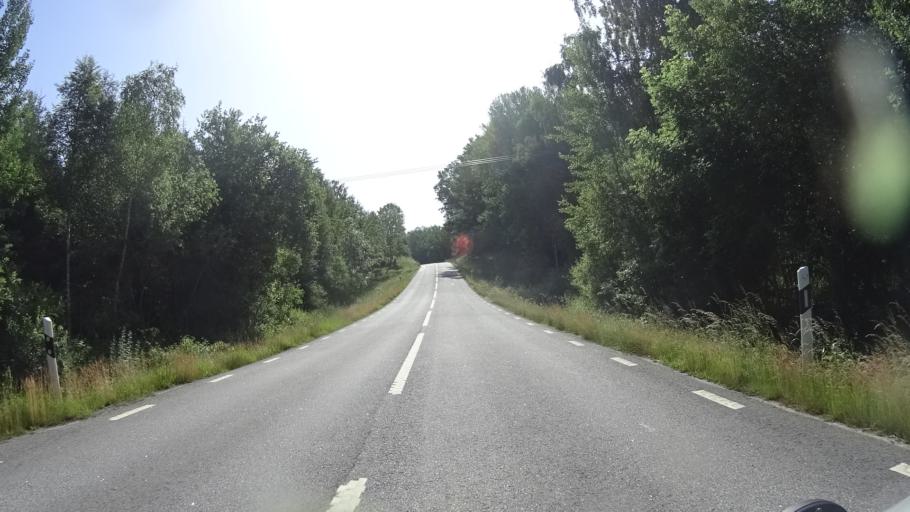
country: SE
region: Kalmar
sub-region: Vasterviks Kommun
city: Overum
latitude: 58.0787
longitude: 16.1646
